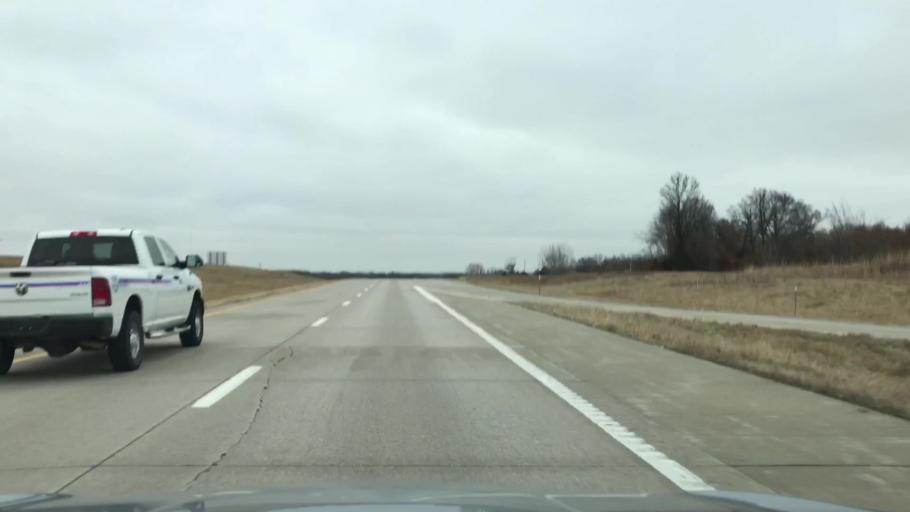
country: US
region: Missouri
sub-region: Linn County
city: Marceline
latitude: 39.7652
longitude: -92.7450
